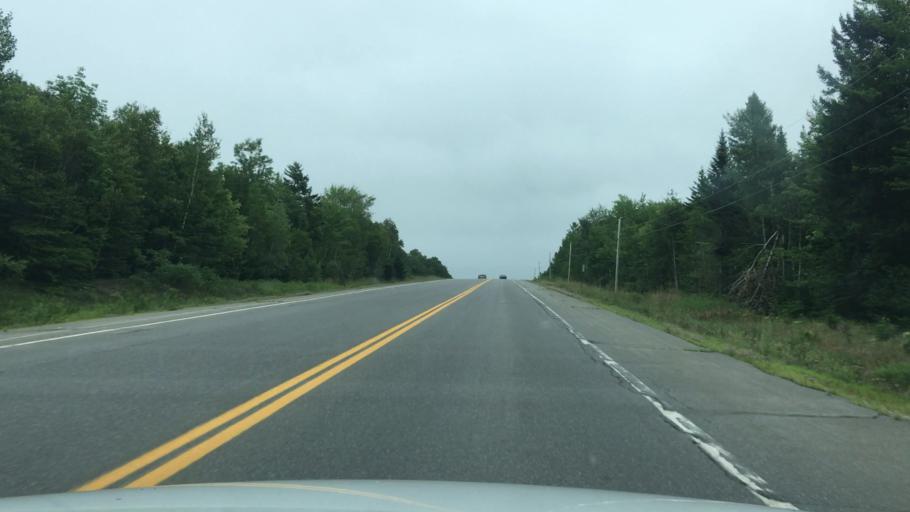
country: US
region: Maine
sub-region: Hancock County
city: Franklin
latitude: 44.8287
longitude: -68.1264
